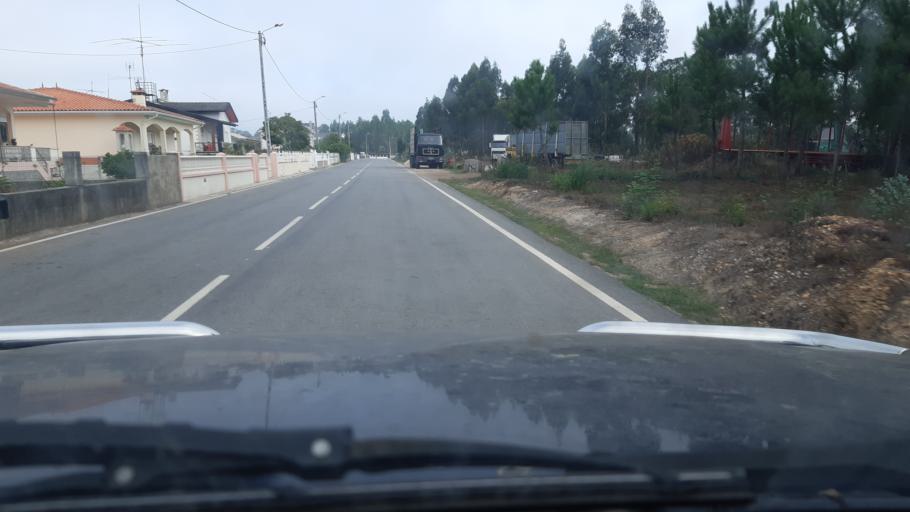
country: PT
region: Aveiro
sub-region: Agueda
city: Agueda
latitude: 40.5829
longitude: -8.4565
